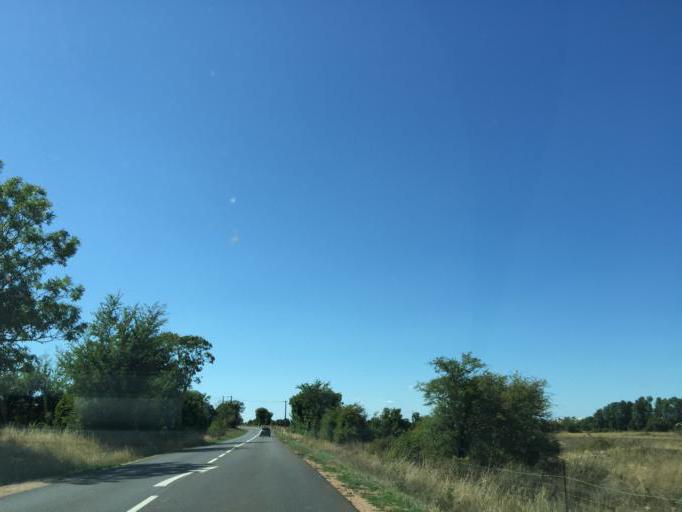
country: FR
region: Midi-Pyrenees
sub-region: Departement de l'Aveyron
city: La Cavalerie
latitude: 44.0147
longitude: 3.1170
